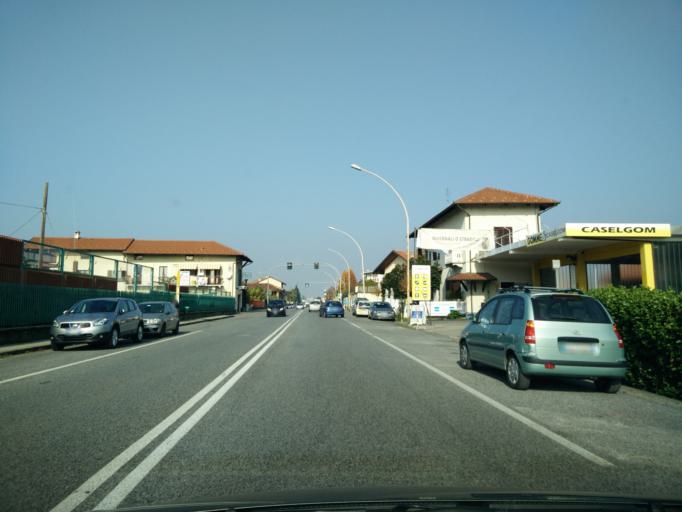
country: IT
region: Piedmont
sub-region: Provincia di Torino
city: Caselle Torinese
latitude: 45.1755
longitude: 7.6507
